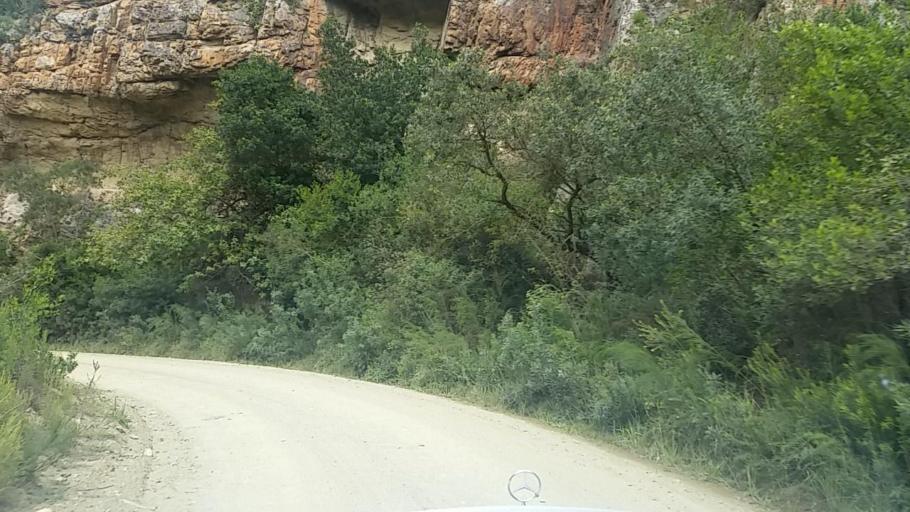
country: ZA
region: Western Cape
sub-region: Eden District Municipality
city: Knysna
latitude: -33.8063
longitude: 23.1805
